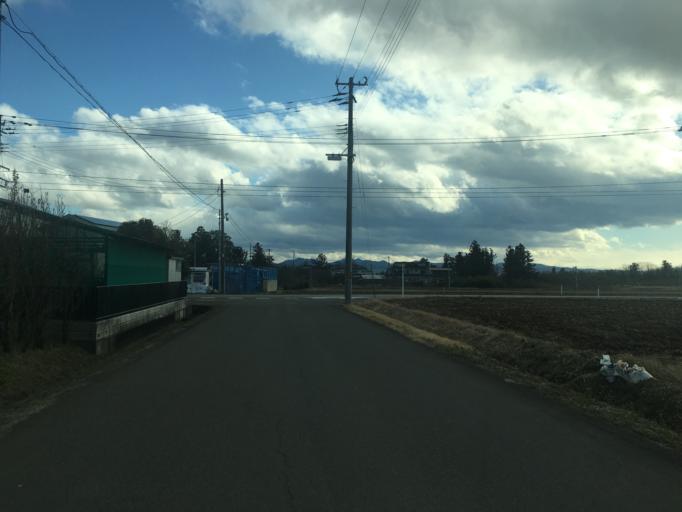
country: JP
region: Fukushima
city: Yanagawamachi-saiwaicho
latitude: 37.8776
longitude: 140.5879
